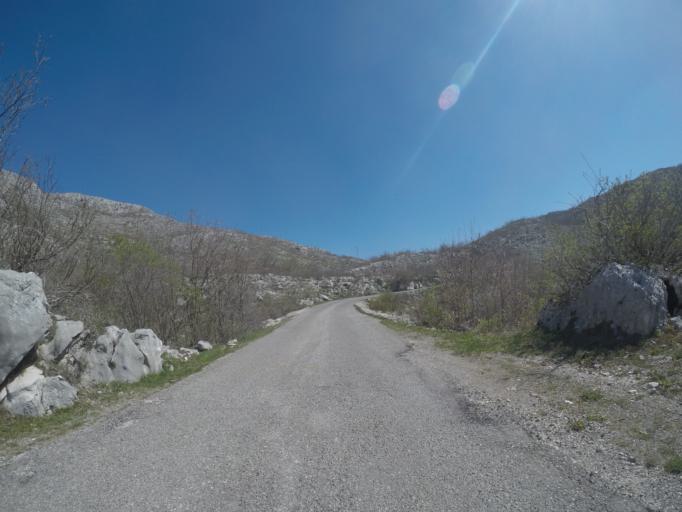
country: ME
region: Cetinje
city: Cetinje
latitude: 42.4970
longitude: 18.8777
